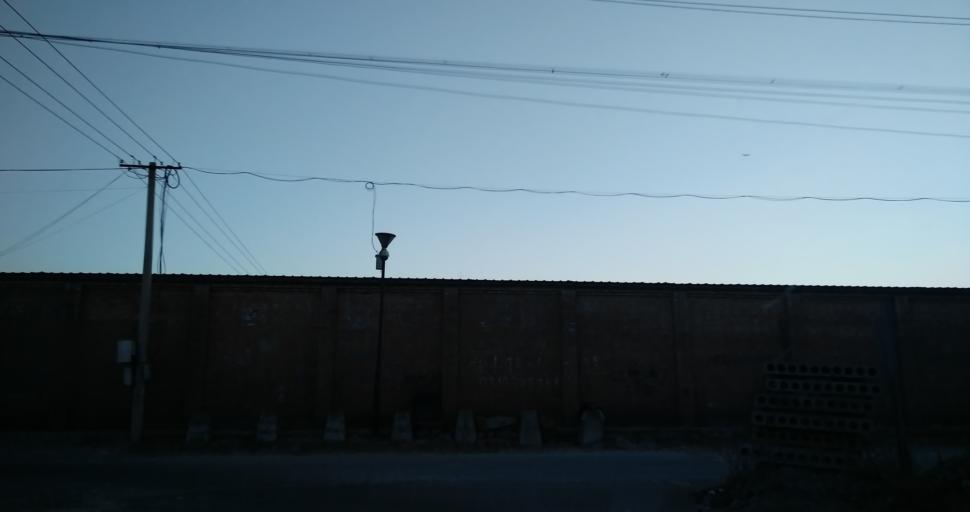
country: CN
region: Beijing
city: Yinghai
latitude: 39.7234
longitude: 116.4695
